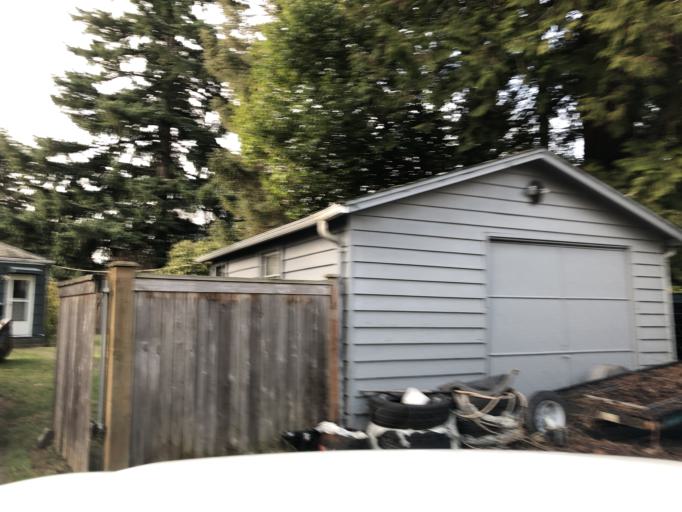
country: US
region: Washington
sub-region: King County
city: Lake Forest Park
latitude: 47.7135
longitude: -122.2817
